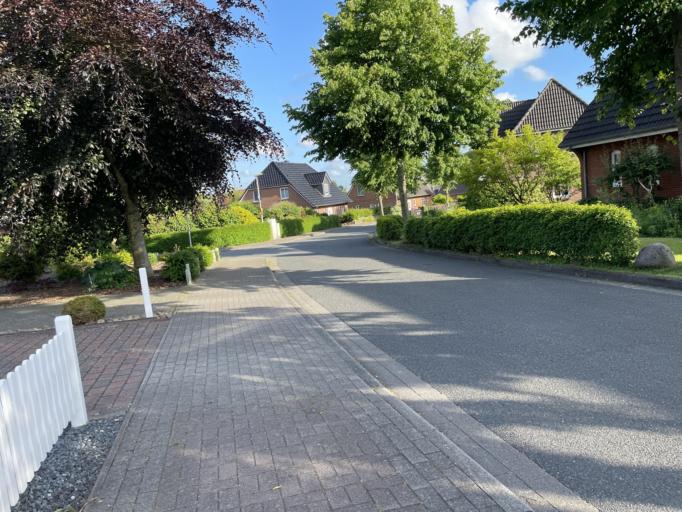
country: DE
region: Schleswig-Holstein
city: Mildstedt
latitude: 54.4578
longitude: 9.1007
